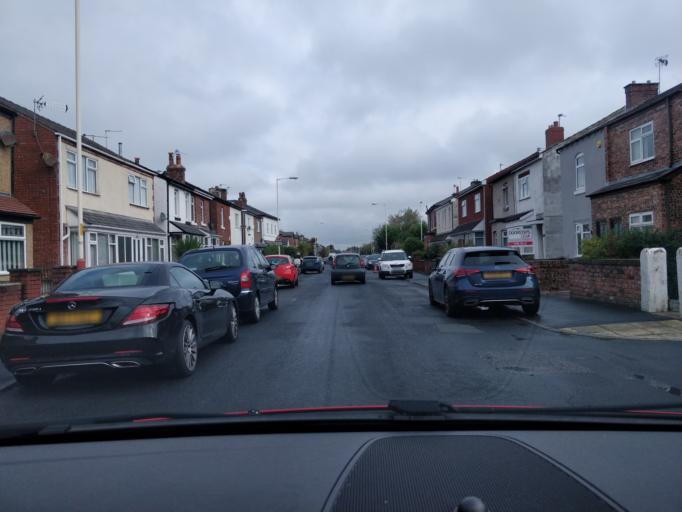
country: GB
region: England
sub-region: Sefton
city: Southport
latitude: 53.6373
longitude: -3.0054
